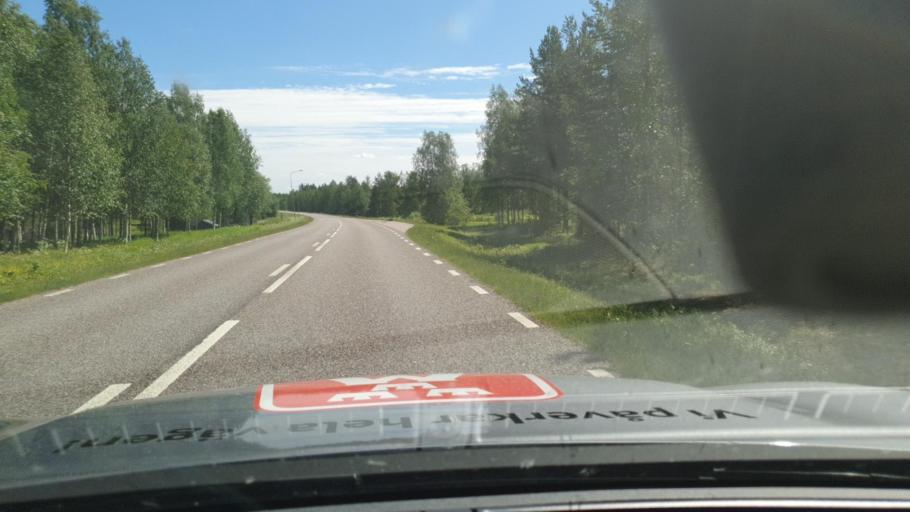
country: FI
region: Lapland
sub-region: Torniolaakso
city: Pello
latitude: 66.9999
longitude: 23.7585
